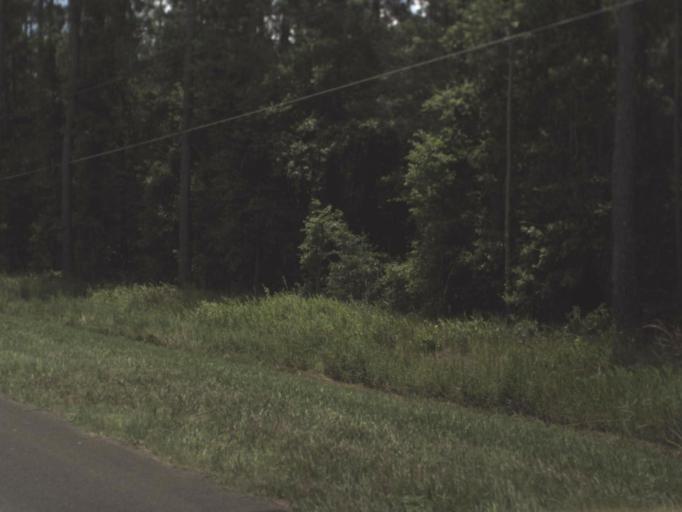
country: US
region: Florida
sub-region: Alachua County
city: Alachua
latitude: 29.7718
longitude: -82.3686
